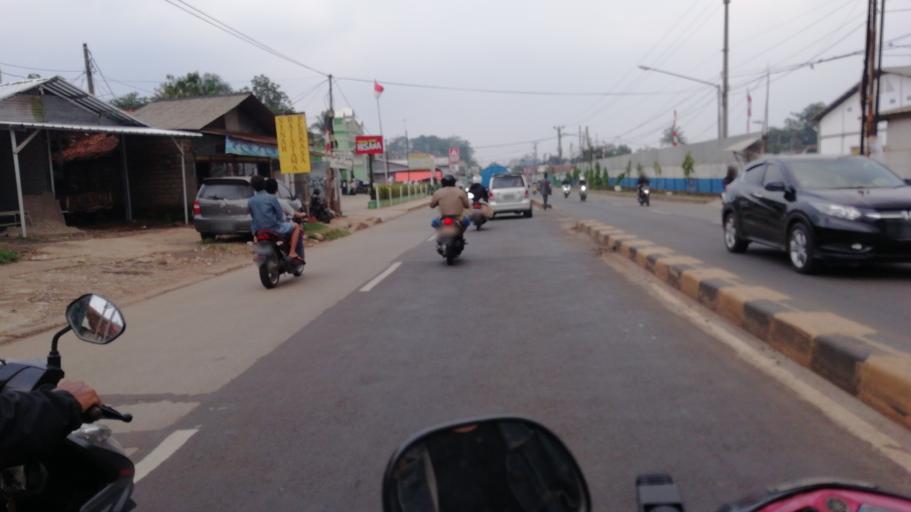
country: ID
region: West Java
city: Parung
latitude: -6.4593
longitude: 106.7304
